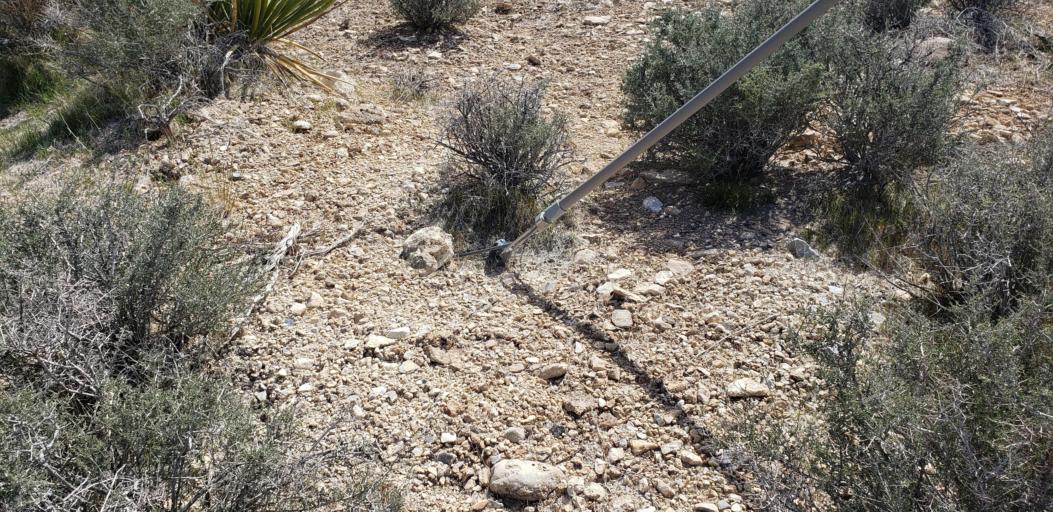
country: US
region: California
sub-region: San Bernardino County
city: Lucerne Valley
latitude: 34.3615
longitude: -116.9073
